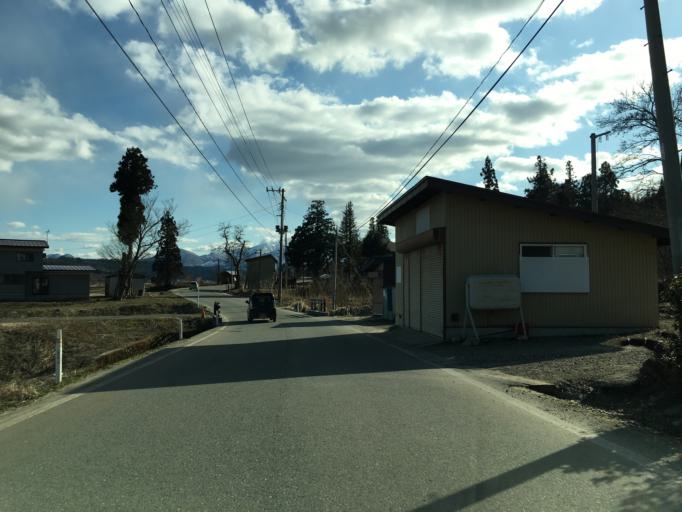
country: JP
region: Yamagata
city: Yonezawa
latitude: 37.9675
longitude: 139.9920
